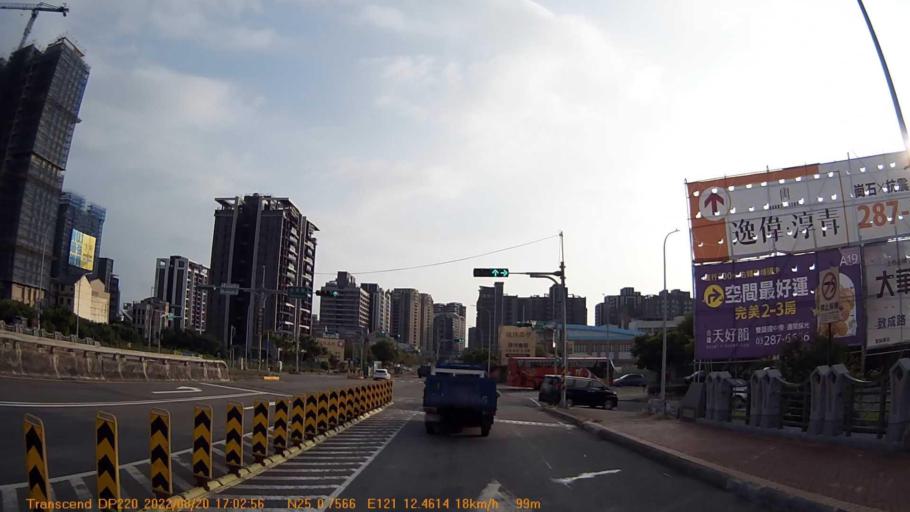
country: TW
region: Taiwan
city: Taoyuan City
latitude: 25.0124
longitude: 121.2075
